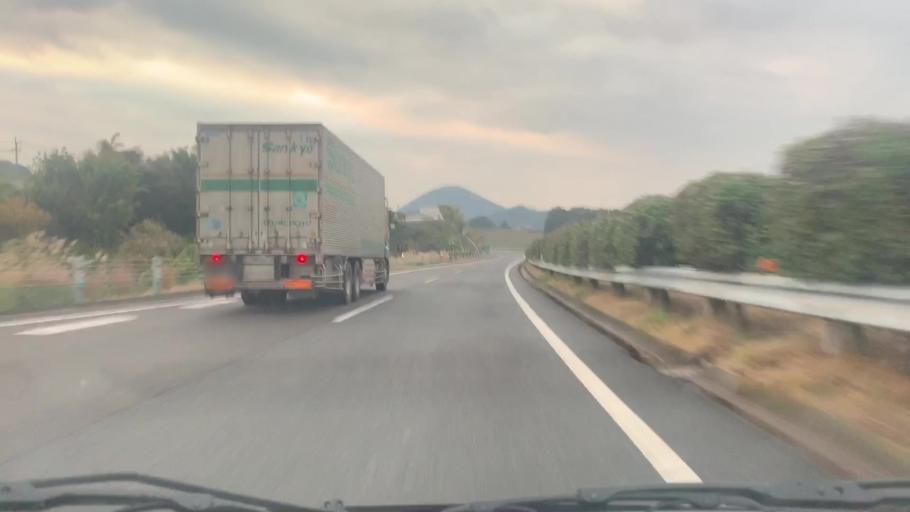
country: JP
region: Nagasaki
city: Omura
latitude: 33.0147
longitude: 129.9500
